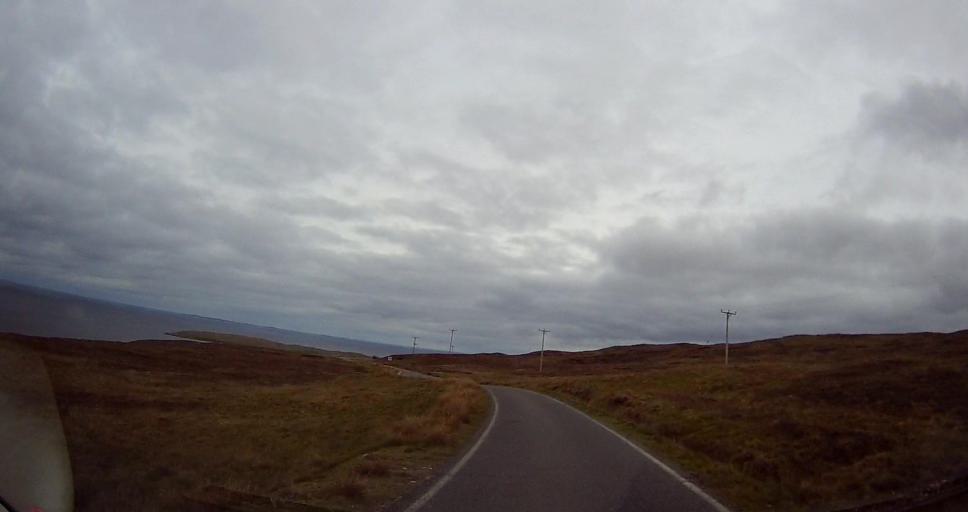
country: GB
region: Scotland
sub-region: Shetland Islands
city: Shetland
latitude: 60.5446
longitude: -1.0553
